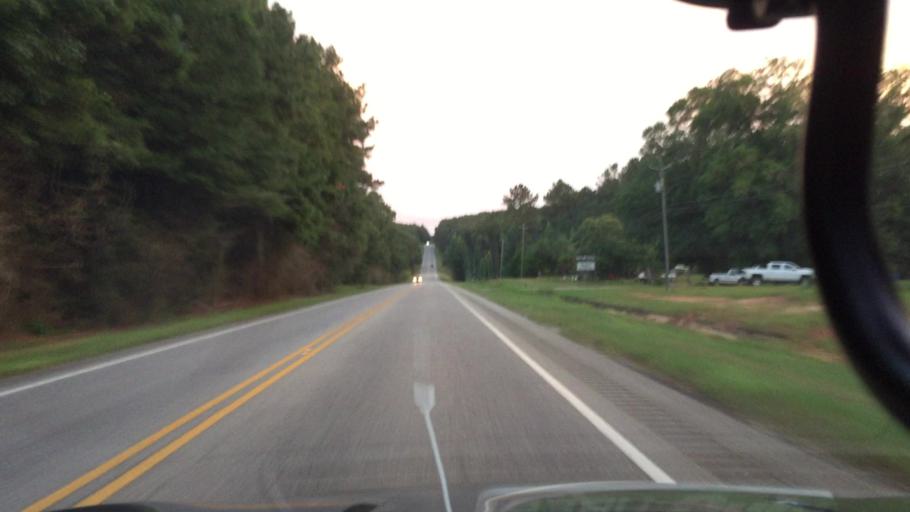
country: US
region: Alabama
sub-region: Coffee County
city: New Brockton
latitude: 31.3874
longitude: -85.8757
